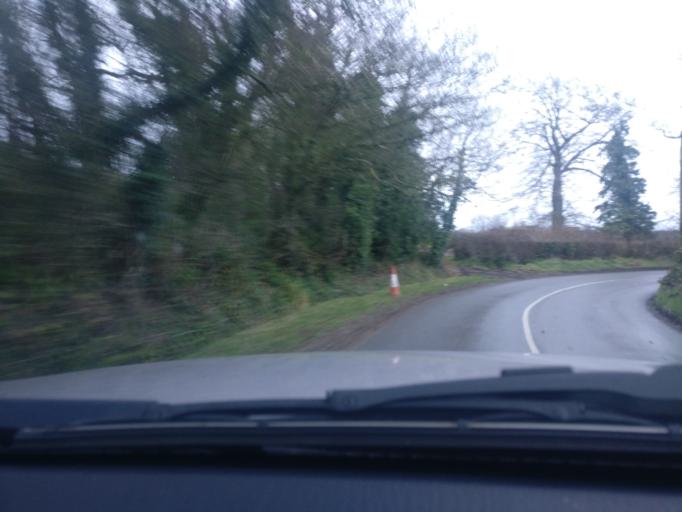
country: IE
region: Leinster
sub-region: Kildare
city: Kilcock
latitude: 53.4712
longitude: -6.6234
